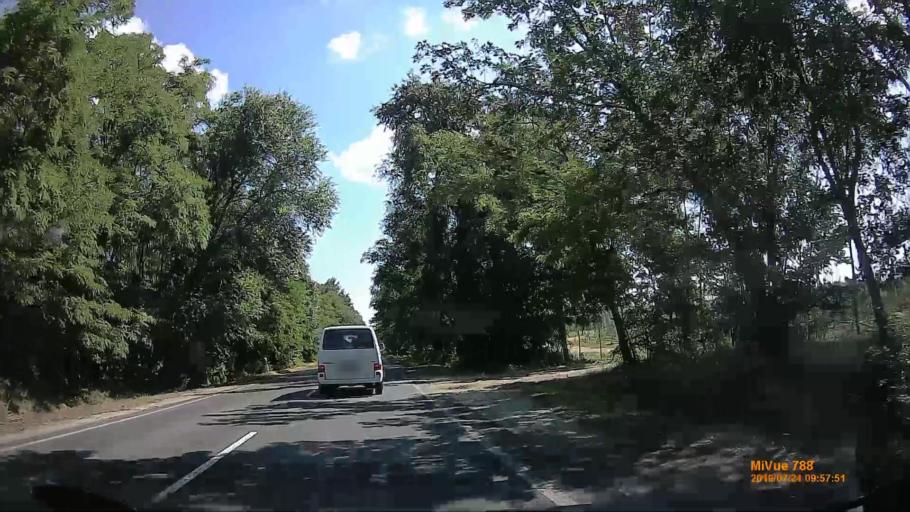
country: HU
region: Szabolcs-Szatmar-Bereg
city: Nyirmada
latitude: 48.0763
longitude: 22.2478
